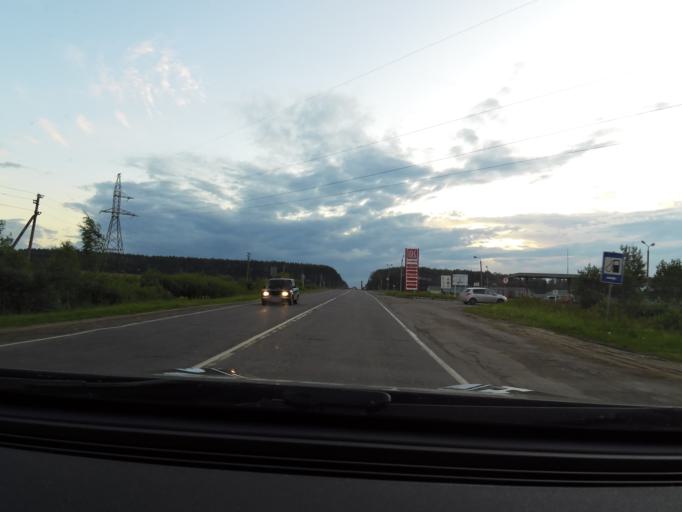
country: RU
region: Vladimir
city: Belaya Rechka
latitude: 56.2829
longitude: 39.3956
